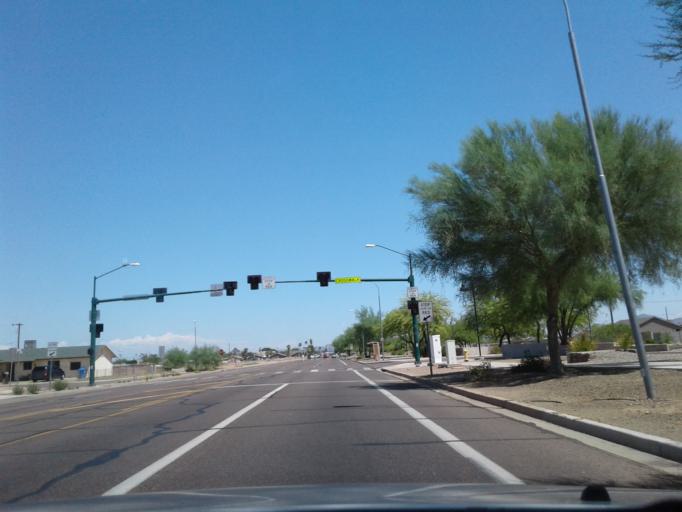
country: US
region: Arizona
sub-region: Maricopa County
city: Phoenix
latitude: 33.4026
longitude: -112.0298
